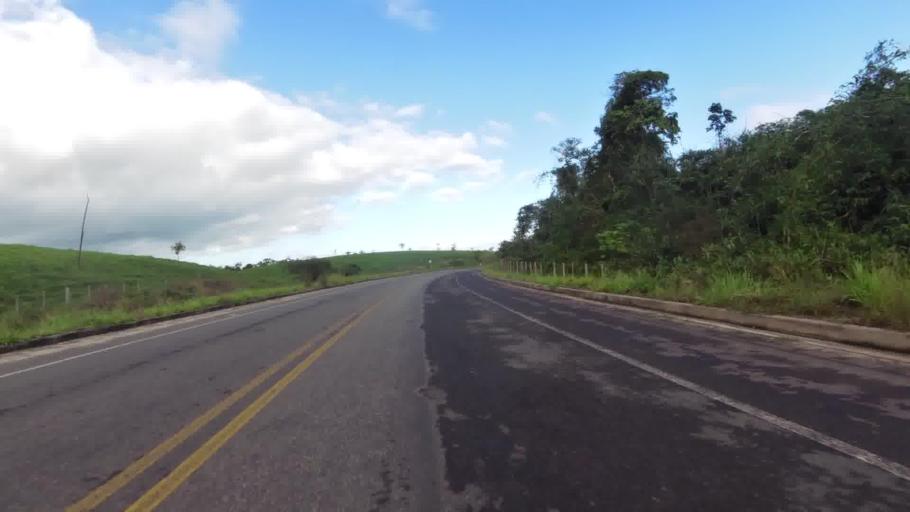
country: BR
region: Espirito Santo
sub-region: Piuma
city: Piuma
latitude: -20.7949
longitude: -40.6141
